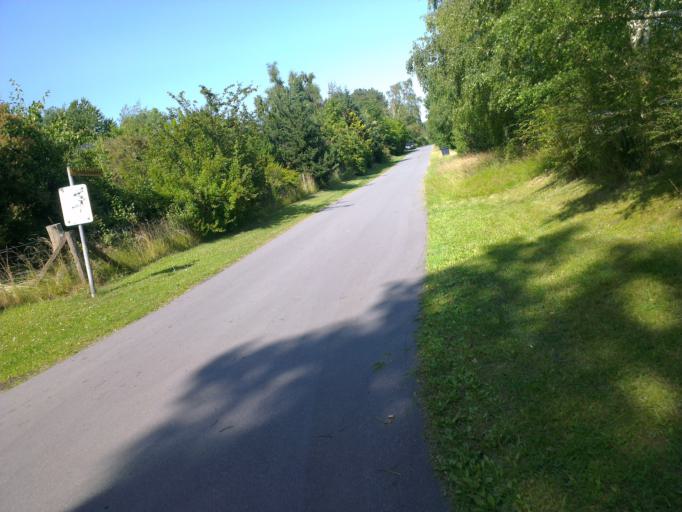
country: DK
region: Capital Region
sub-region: Halsnaes Kommune
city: Hundested
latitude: 55.9235
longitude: 11.9162
